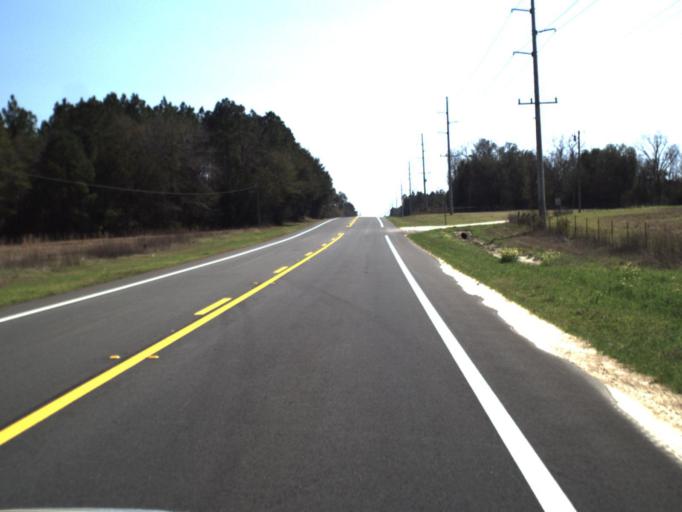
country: US
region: Florida
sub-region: Jackson County
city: Sneads
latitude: 30.8019
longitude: -85.0324
